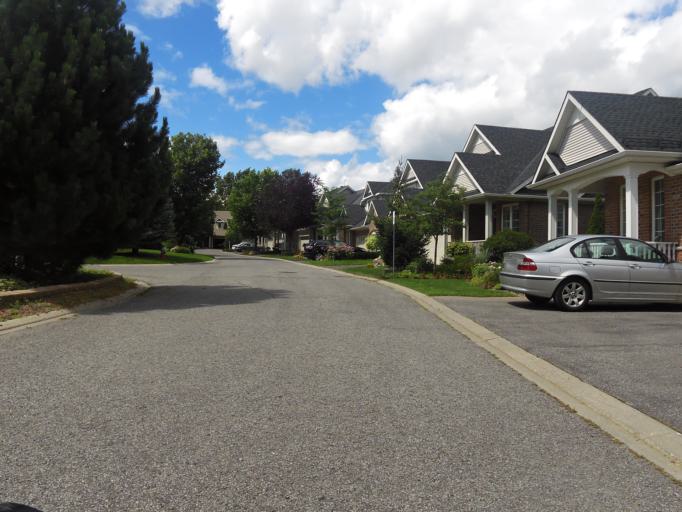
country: CA
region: Ontario
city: Bells Corners
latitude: 45.3171
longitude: -75.9012
